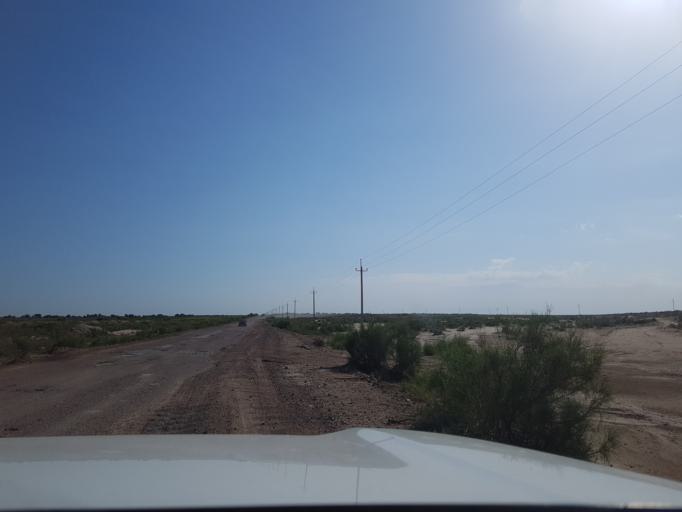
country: TM
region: Dasoguz
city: Koeneuergench
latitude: 42.0304
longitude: 58.8016
